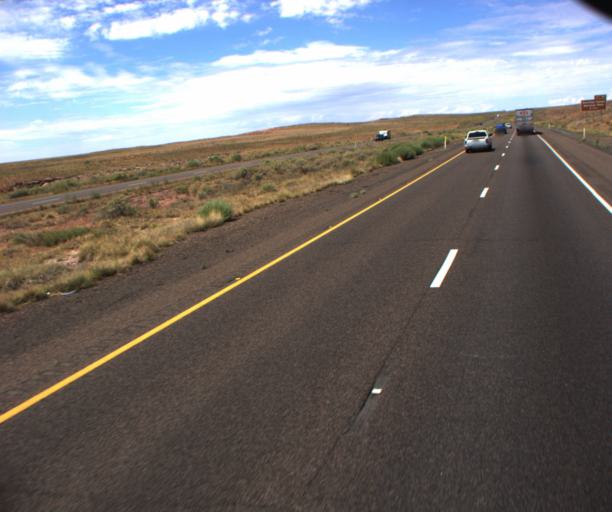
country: US
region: Arizona
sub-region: Navajo County
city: Holbrook
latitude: 35.0740
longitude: -109.7435
